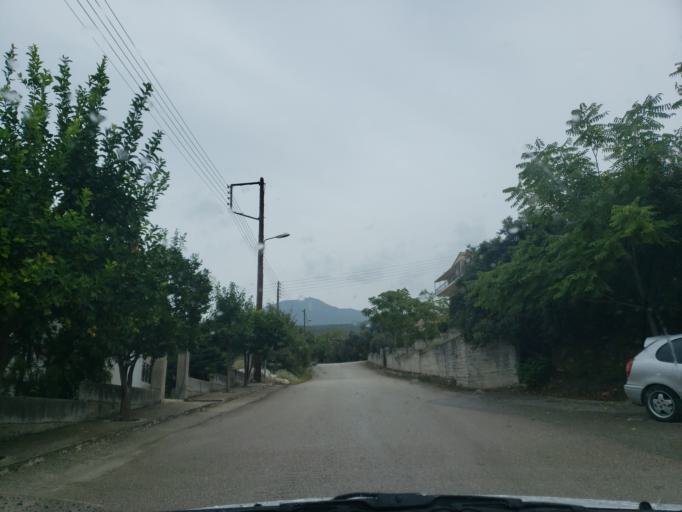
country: GR
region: Central Greece
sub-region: Nomos Fthiotidos
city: Anthili
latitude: 38.7992
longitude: 22.4780
